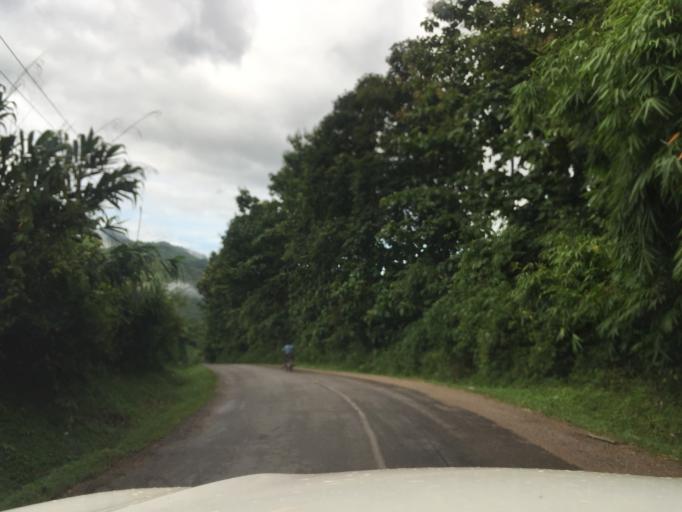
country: LA
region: Oudomxai
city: Muang La
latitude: 20.8011
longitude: 102.0872
